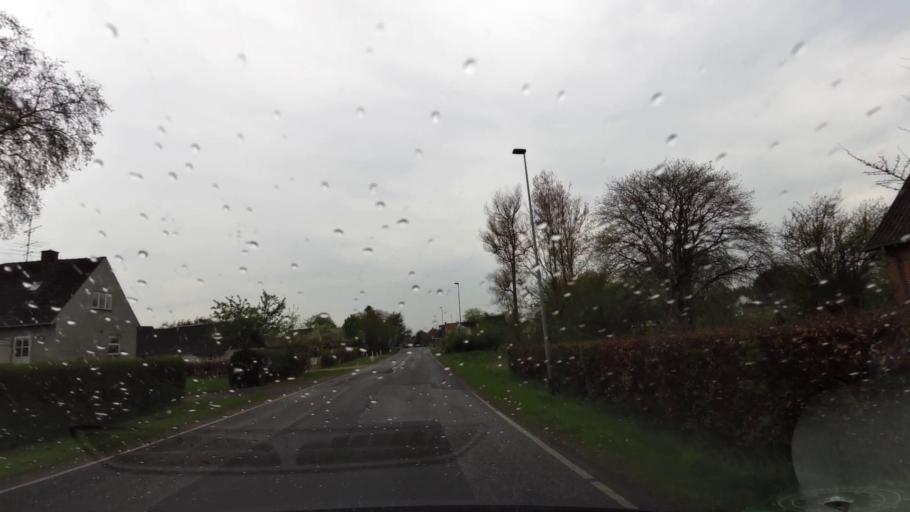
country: DK
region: South Denmark
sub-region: Faaborg-Midtfyn Kommune
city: Ringe
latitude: 55.1930
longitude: 10.5472
